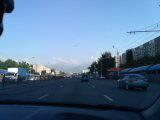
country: KZ
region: Almaty Qalasy
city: Almaty
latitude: 43.2448
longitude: 76.8348
